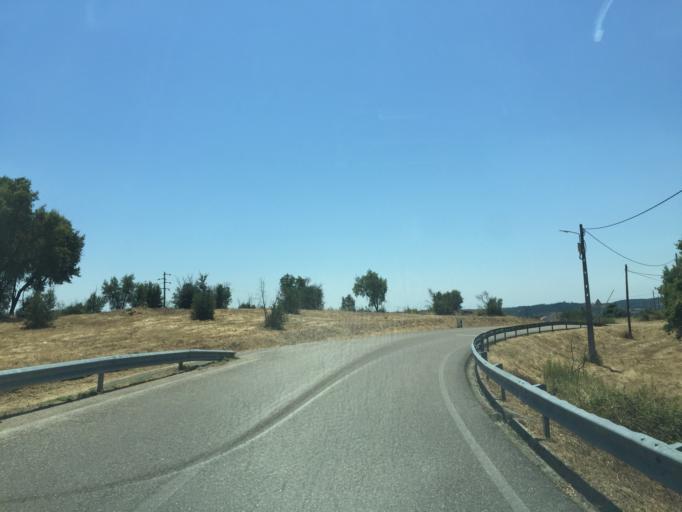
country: PT
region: Santarem
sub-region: Constancia
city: Constancia
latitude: 39.5757
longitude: -8.2948
